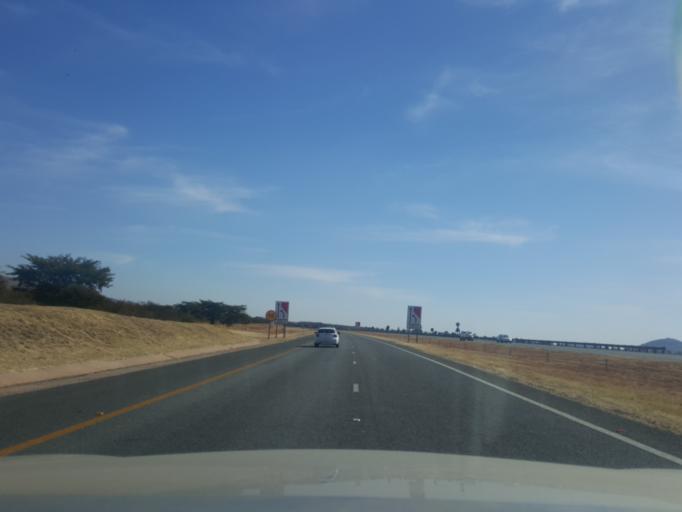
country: ZA
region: North-West
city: Ga-Rankuwa
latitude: -25.6554
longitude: 28.0396
